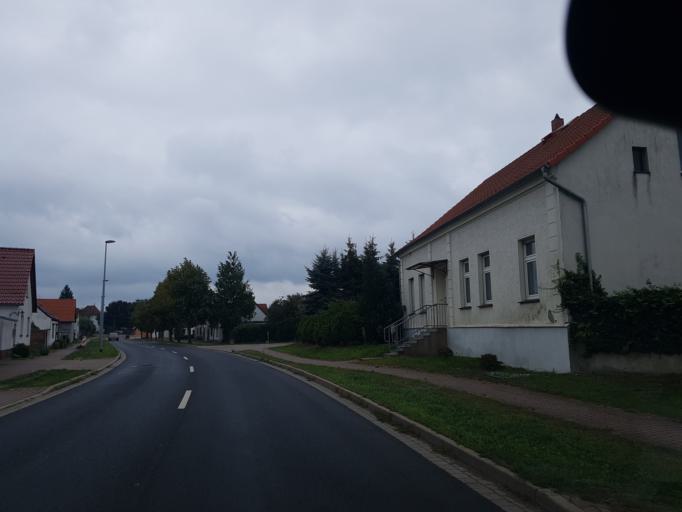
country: DE
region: Saxony-Anhalt
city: Tucheim
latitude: 52.3083
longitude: 12.0922
